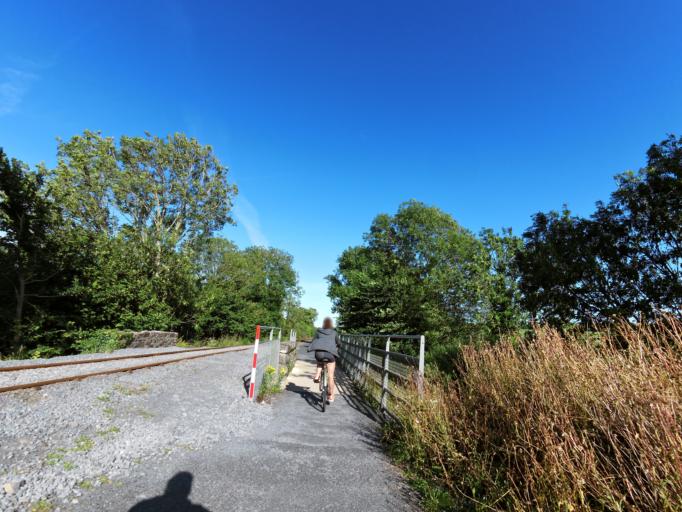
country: IE
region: Leinster
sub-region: Kilkenny
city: Mooncoin
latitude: 52.2471
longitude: -7.2352
